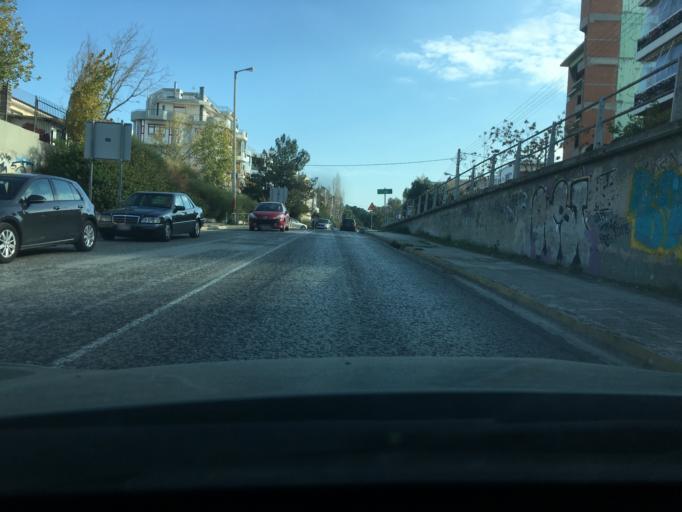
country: GR
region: Attica
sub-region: Nomarchia Athinas
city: Khalandrion
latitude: 38.0317
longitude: 23.7952
